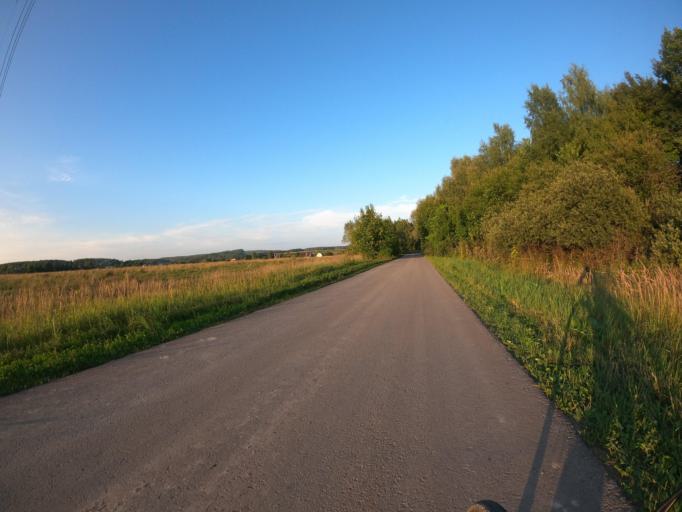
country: RU
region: Moskovskaya
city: Malino
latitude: 55.0952
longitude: 38.2878
